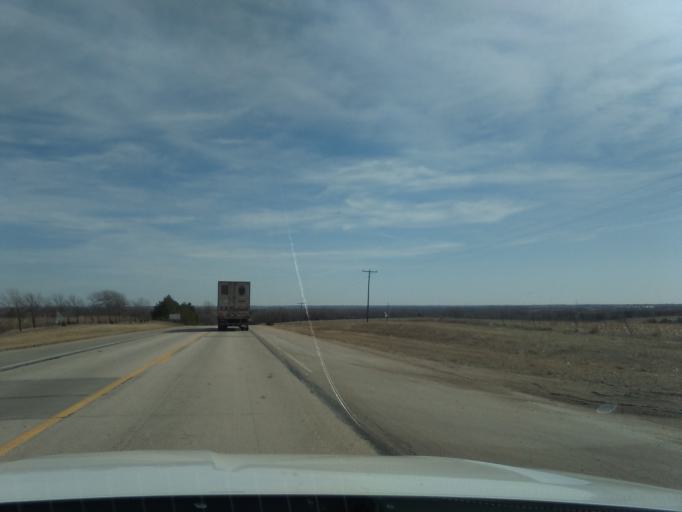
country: US
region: Nebraska
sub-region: Lancaster County
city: Hickman
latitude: 40.6538
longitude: -96.7810
